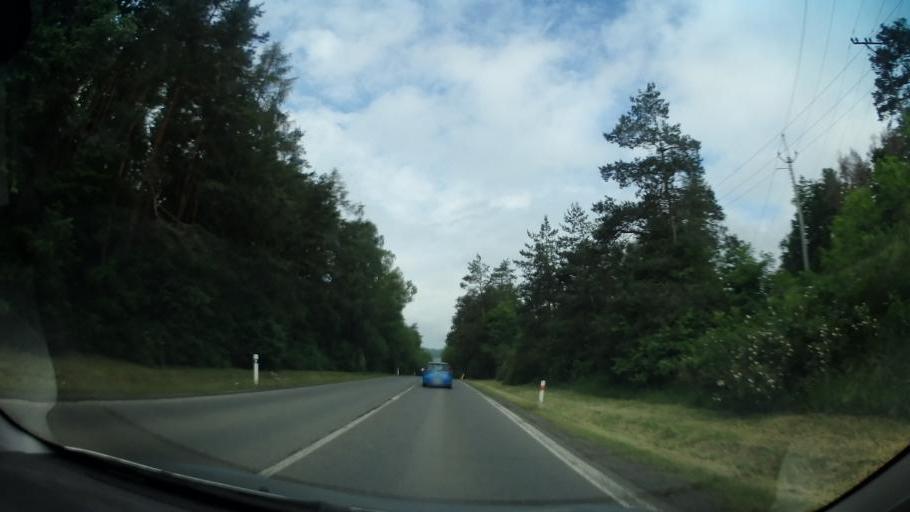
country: CZ
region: South Moravian
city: Cebin
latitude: 49.3092
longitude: 16.4969
